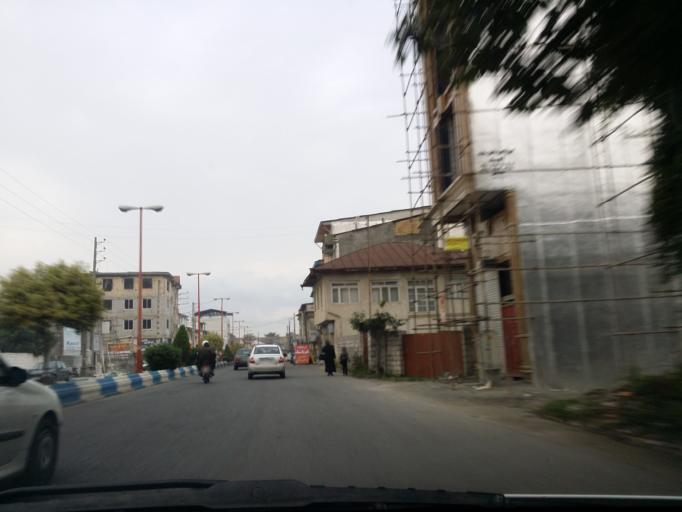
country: IR
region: Mazandaran
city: `Abbasabad
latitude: 36.7251
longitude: 51.1043
